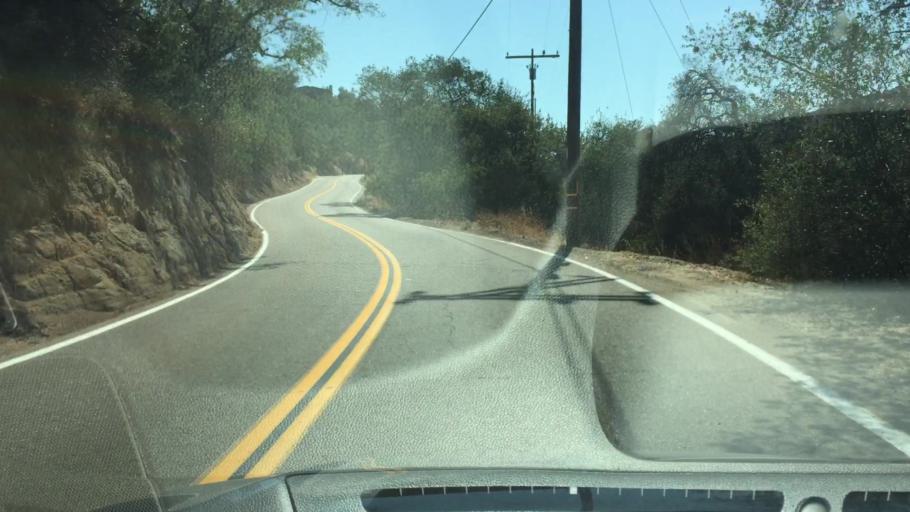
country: US
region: California
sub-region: San Diego County
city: Harbison Canyon
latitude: 32.7482
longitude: -116.7934
